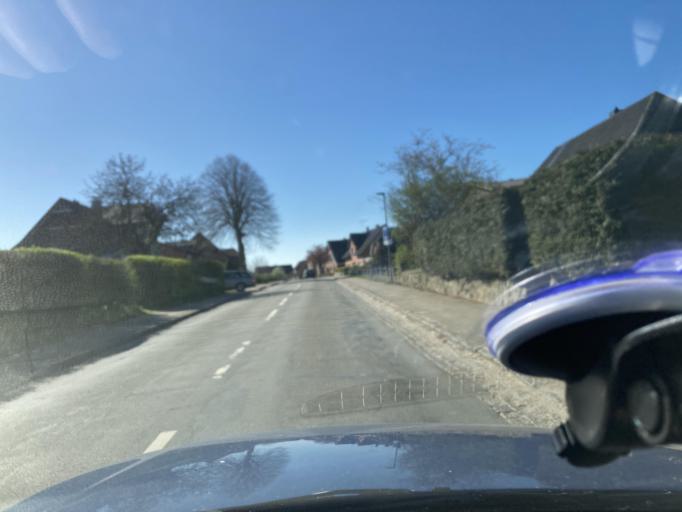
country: DE
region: Schleswig-Holstein
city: Nordhastedt
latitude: 54.1721
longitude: 9.1894
